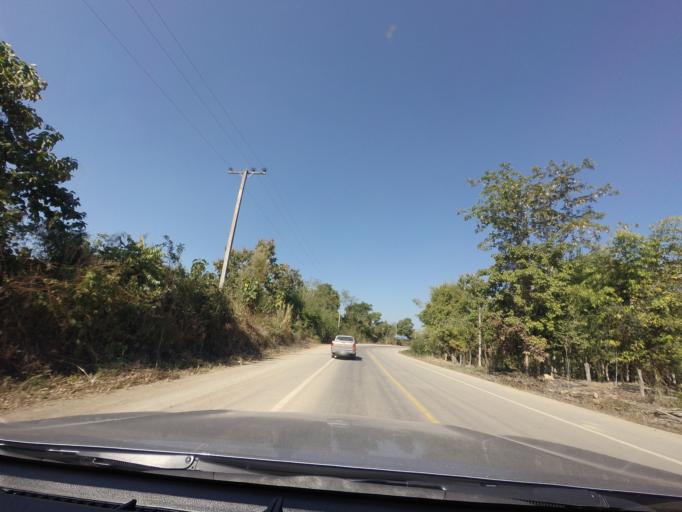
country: TH
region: Lampang
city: Chae Hom
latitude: 18.5245
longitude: 99.6431
